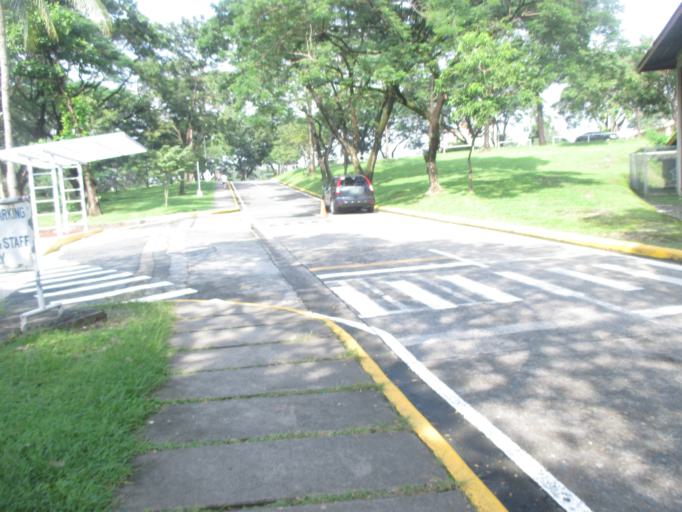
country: PH
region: Metro Manila
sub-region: Marikina
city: Calumpang
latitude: 14.6365
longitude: 121.0786
